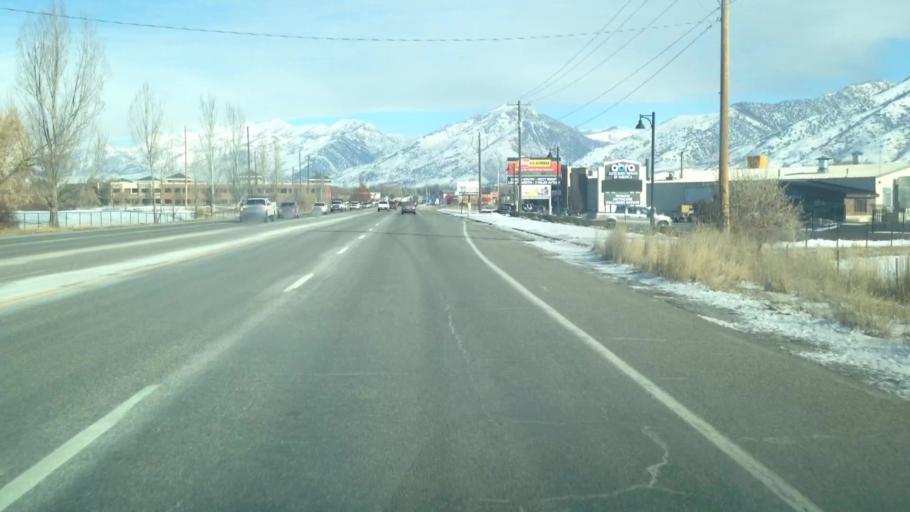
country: US
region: Utah
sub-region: Cache County
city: River Heights
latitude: 41.7094
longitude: -111.8439
